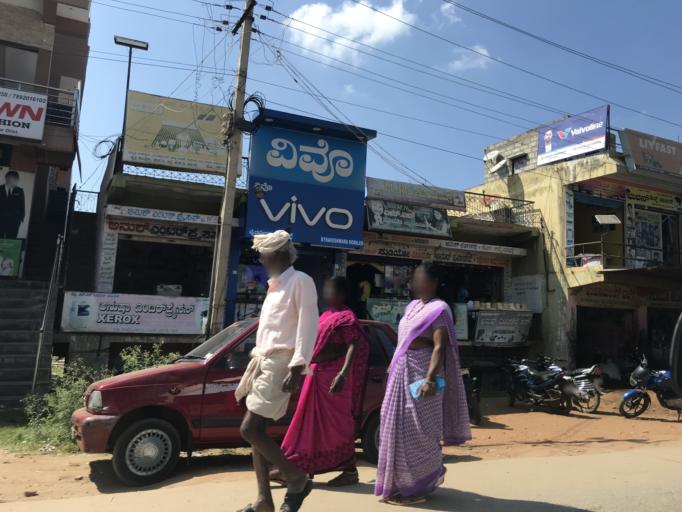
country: IN
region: Karnataka
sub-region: Mysore
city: Heggadadevankote
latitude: 12.0855
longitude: 76.3335
